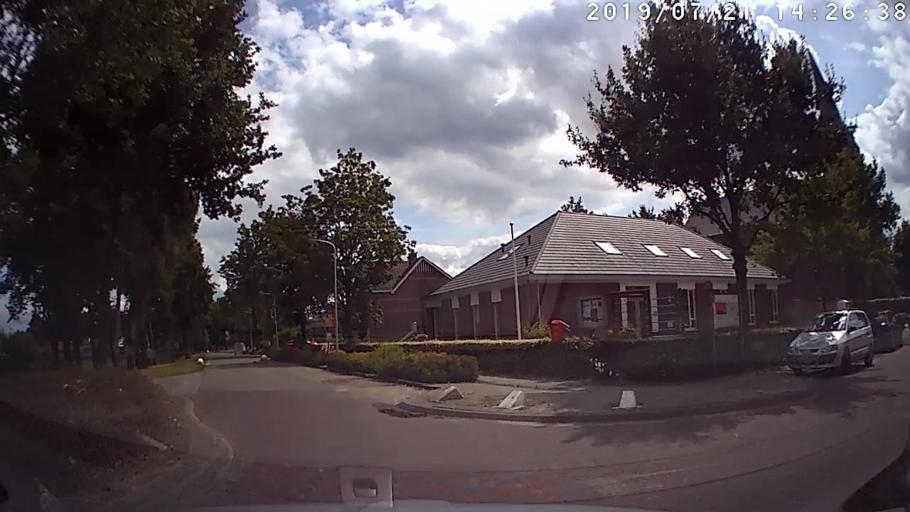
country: NL
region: Overijssel
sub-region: Gemeente Raalte
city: Heino
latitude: 52.4371
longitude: 6.1921
